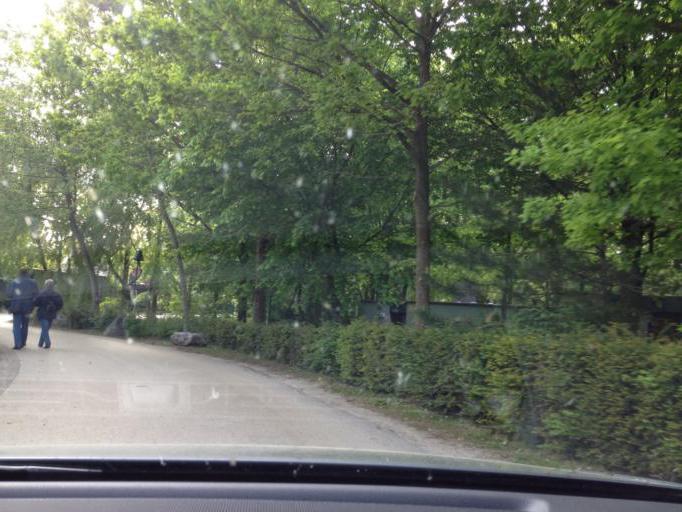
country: NL
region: Utrecht
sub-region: Gemeente Bunschoten
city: Bunschoten
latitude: 52.2613
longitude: 5.4000
